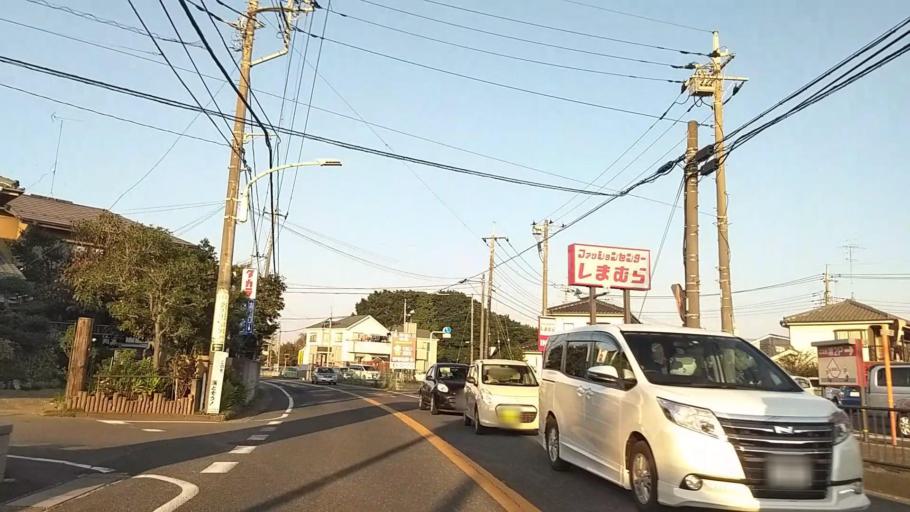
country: JP
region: Saitama
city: Tokorozawa
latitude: 35.8182
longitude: 139.4646
